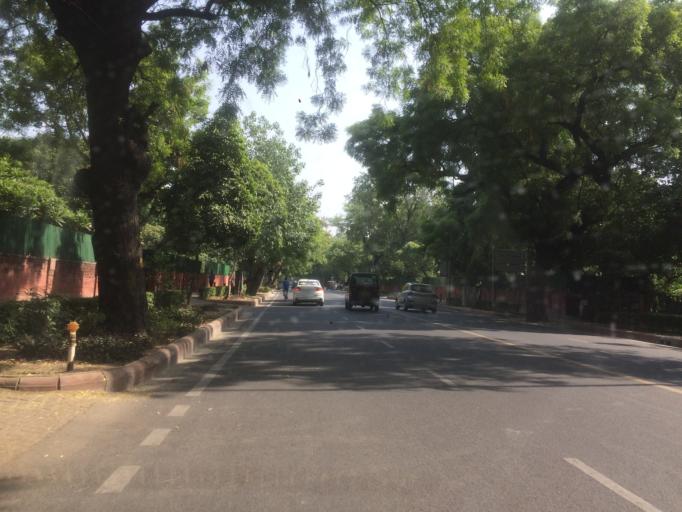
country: IN
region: NCT
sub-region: New Delhi
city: New Delhi
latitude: 28.6038
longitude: 77.2305
